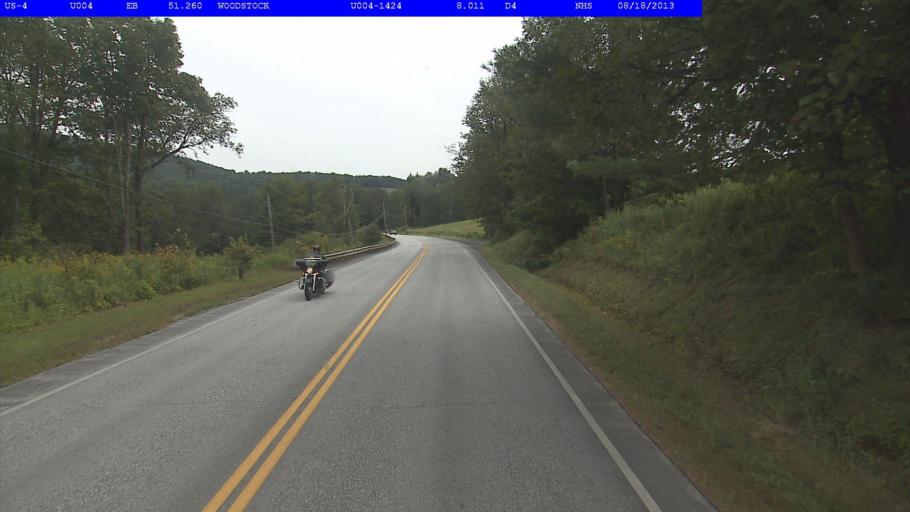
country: US
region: Vermont
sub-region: Windsor County
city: Woodstock
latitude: 43.6370
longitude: -72.4926
